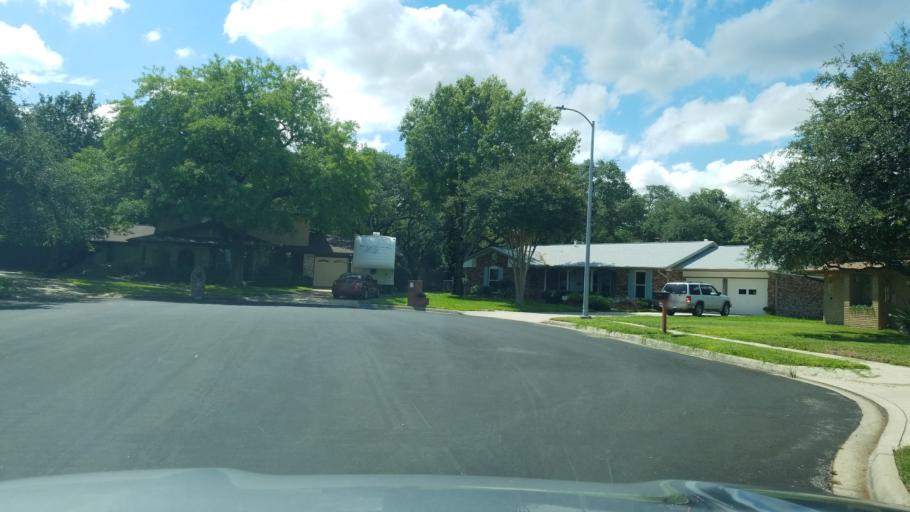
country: US
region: Texas
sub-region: Bexar County
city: Castle Hills
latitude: 29.5470
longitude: -98.5034
